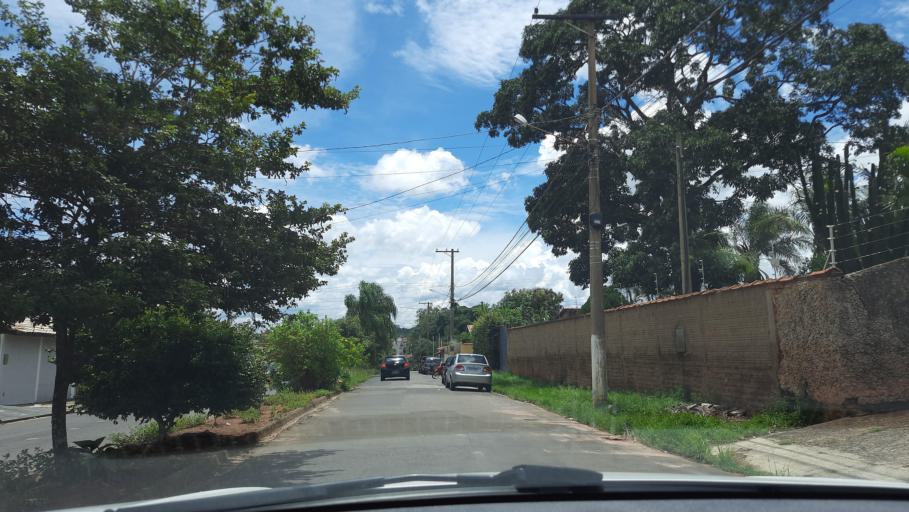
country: BR
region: Sao Paulo
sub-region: Casa Branca
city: Casa Branca
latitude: -21.7838
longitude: -47.0908
